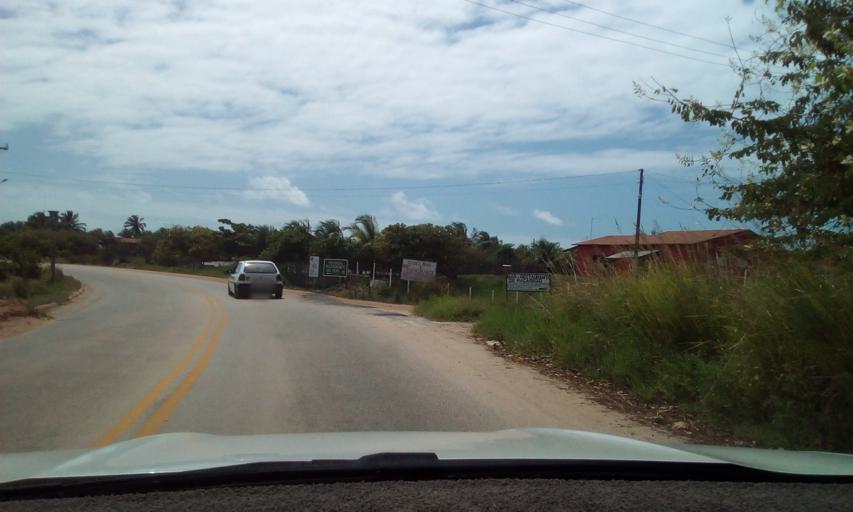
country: BR
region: Paraiba
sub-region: Rio Tinto
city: Rio Tinto
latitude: -6.7078
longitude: -34.9358
